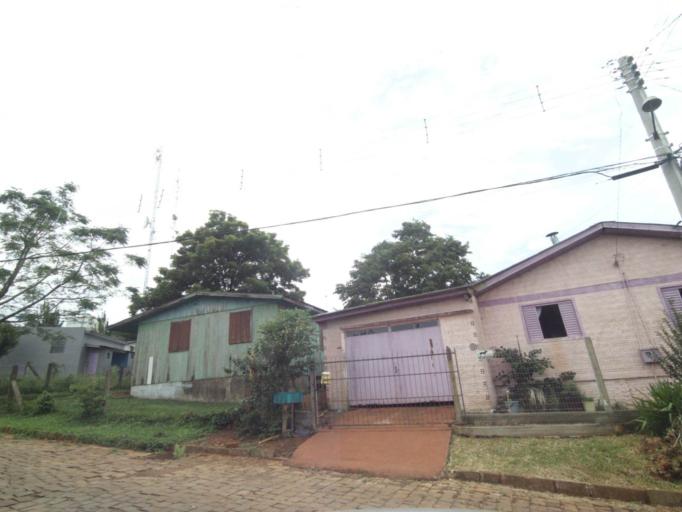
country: BR
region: Rio Grande do Sul
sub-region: Lagoa Vermelha
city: Lagoa Vermelha
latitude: -28.2232
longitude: -51.5132
